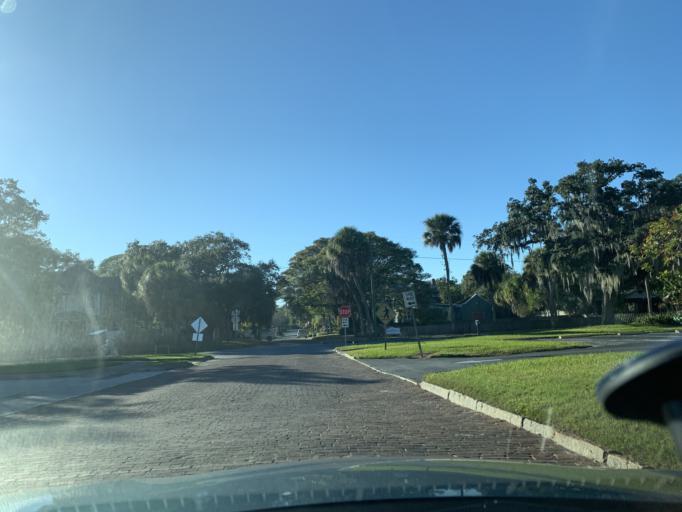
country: US
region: Florida
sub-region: Pinellas County
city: Gulfport
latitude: 27.7434
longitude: -82.7078
